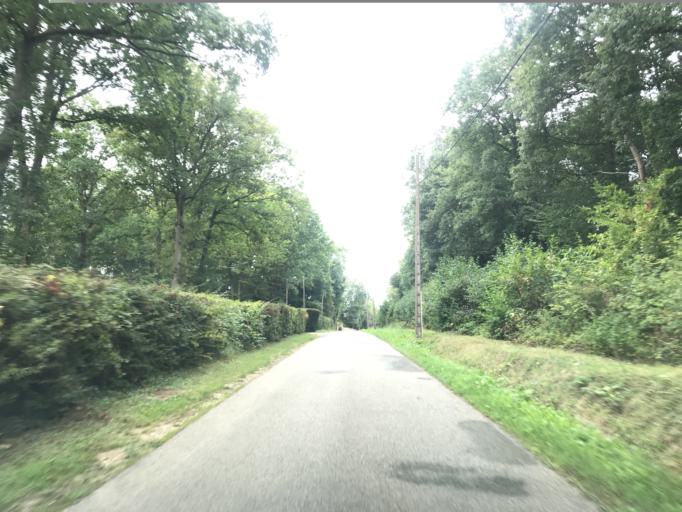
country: FR
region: Haute-Normandie
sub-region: Departement de l'Eure
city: Houlbec-Cocherel
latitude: 49.0566
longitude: 1.3512
